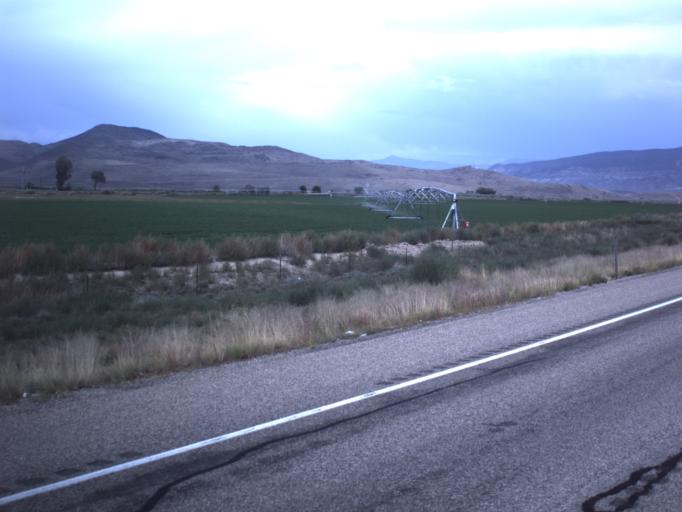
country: US
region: Utah
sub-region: Piute County
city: Junction
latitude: 38.1730
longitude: -112.2586
